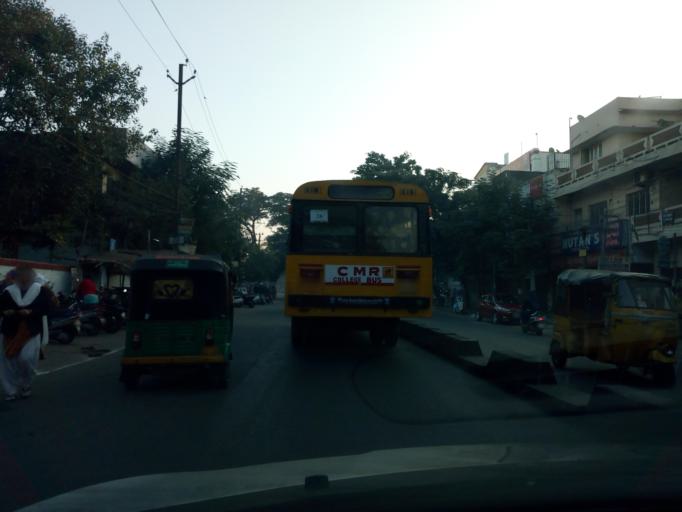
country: IN
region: Telangana
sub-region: Rangareddi
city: Gaddi Annaram
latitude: 17.4003
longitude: 78.5073
